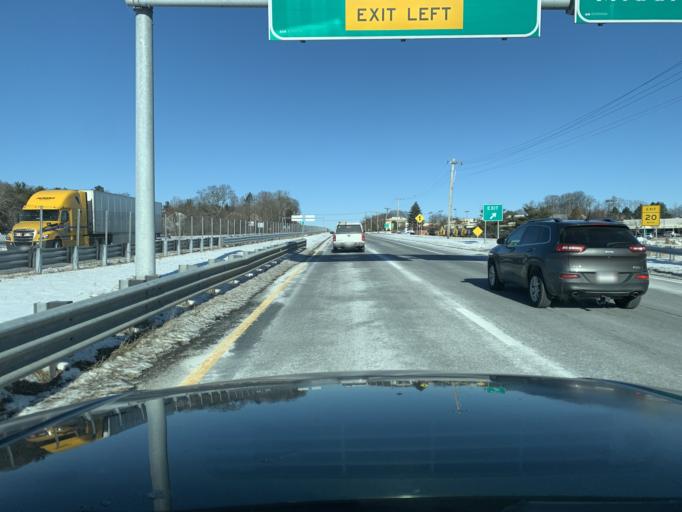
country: US
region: Massachusetts
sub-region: Essex County
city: Danvers
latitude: 42.5841
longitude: -70.9671
